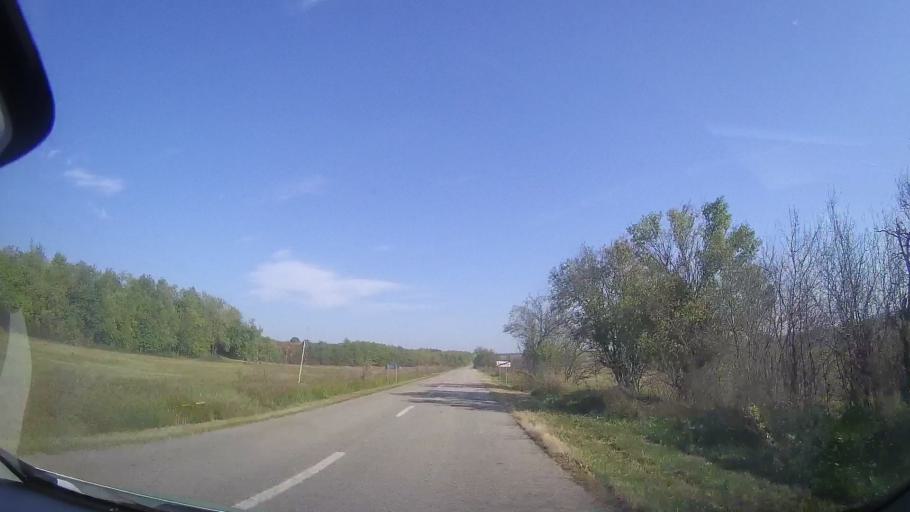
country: RO
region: Timis
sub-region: Comuna Ghizela
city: Ghizela
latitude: 45.8093
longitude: 21.7208
